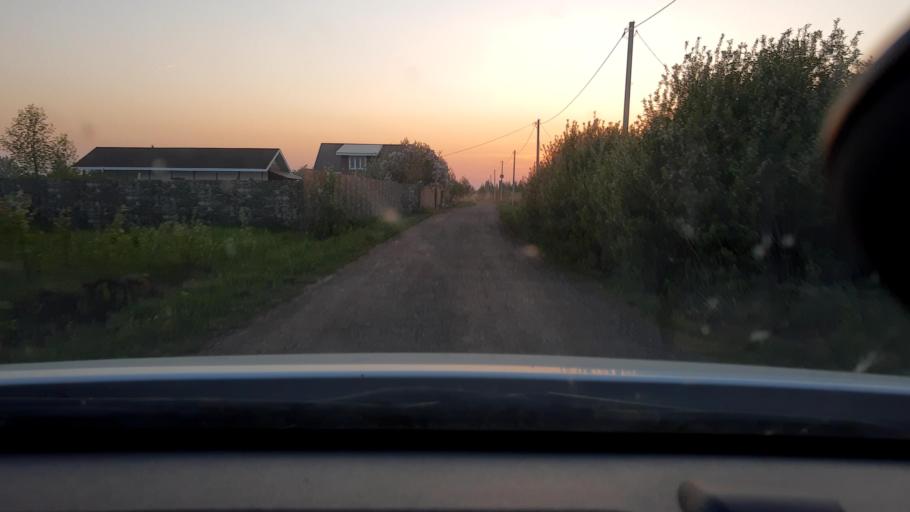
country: RU
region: Bashkortostan
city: Avdon
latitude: 54.5285
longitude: 55.8179
